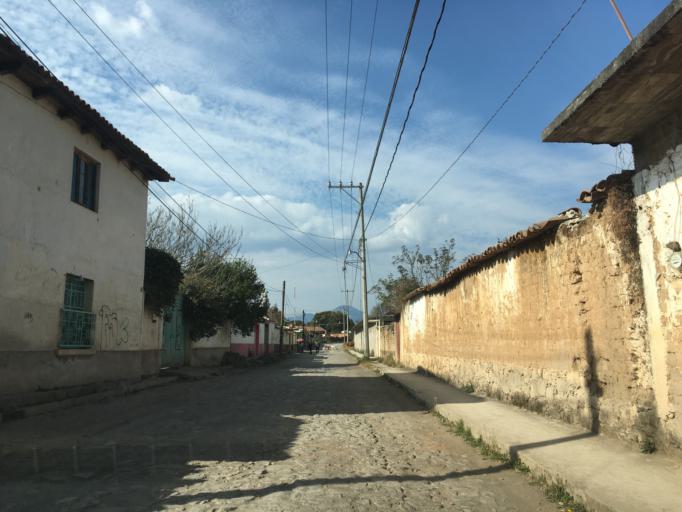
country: MX
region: Michoacan
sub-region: Patzcuaro
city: Santa Ana Chapitiro
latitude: 19.5368
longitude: -101.6323
